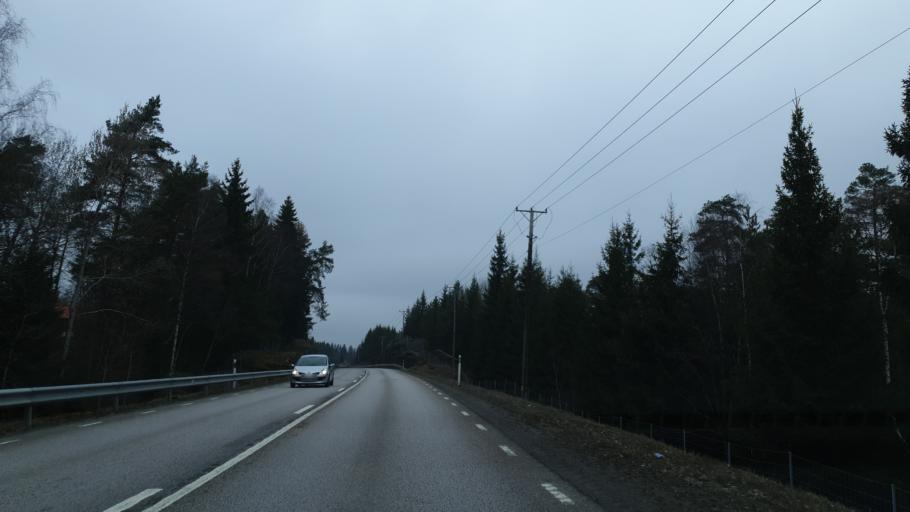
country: SE
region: Vaestra Goetaland
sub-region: Harryda Kommun
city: Hindas
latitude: 57.6361
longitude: 12.4088
